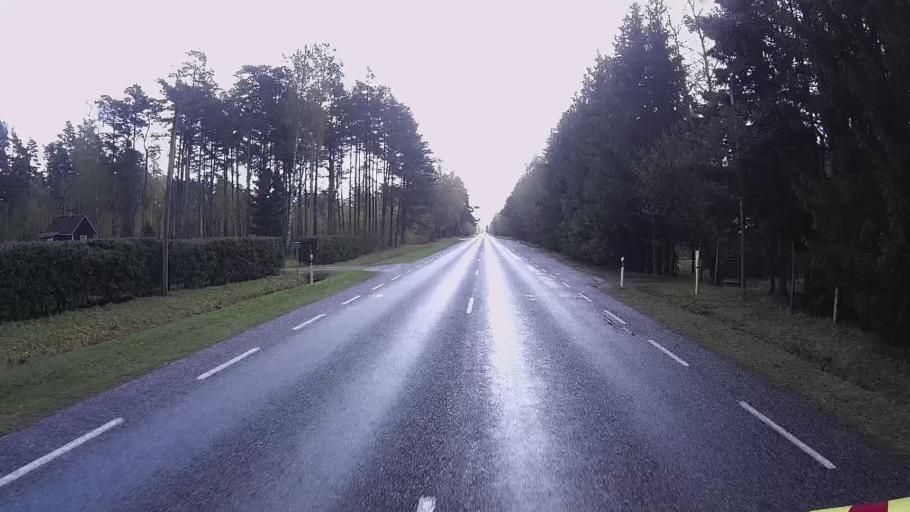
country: EE
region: Hiiumaa
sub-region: Kaerdla linn
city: Kardla
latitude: 58.9473
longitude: 22.8862
